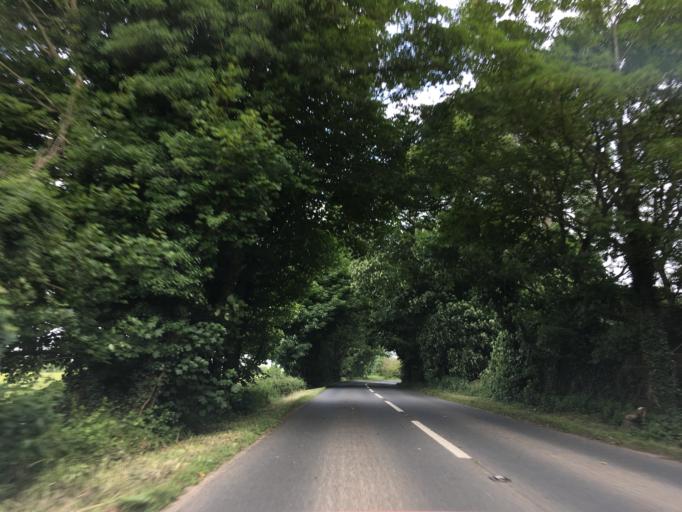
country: GB
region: England
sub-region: Gloucestershire
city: Nailsworth
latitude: 51.6583
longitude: -2.2631
